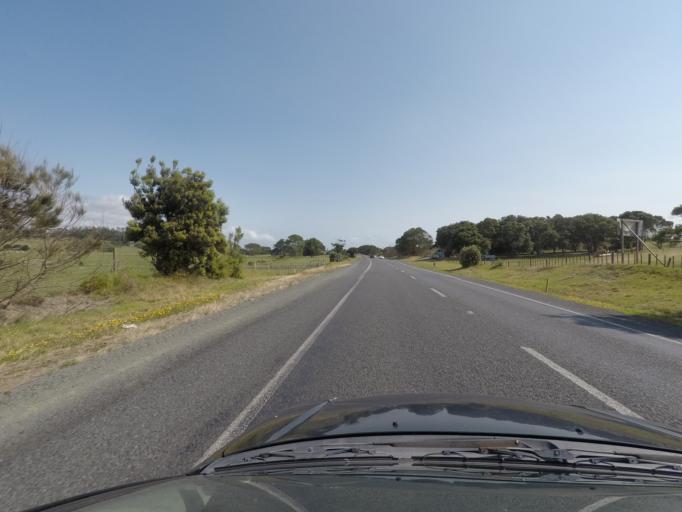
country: NZ
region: Northland
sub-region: Whangarei
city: Ruakaka
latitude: -35.9436
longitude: 174.4556
